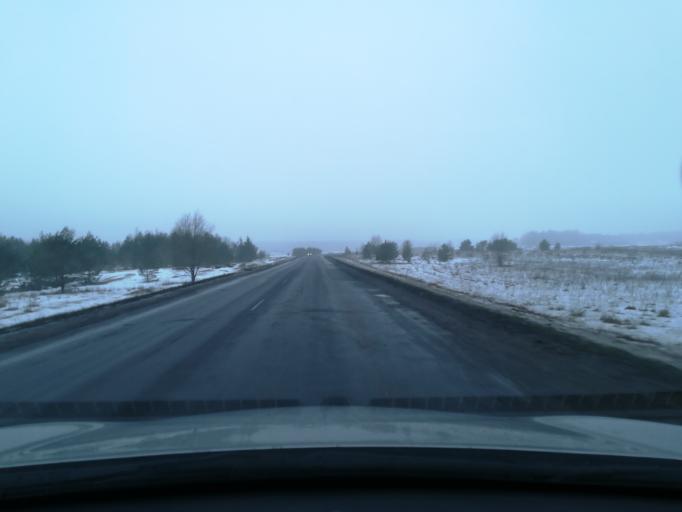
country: EE
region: Harju
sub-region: Raasiku vald
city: Arukula
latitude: 59.3489
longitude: 25.0920
